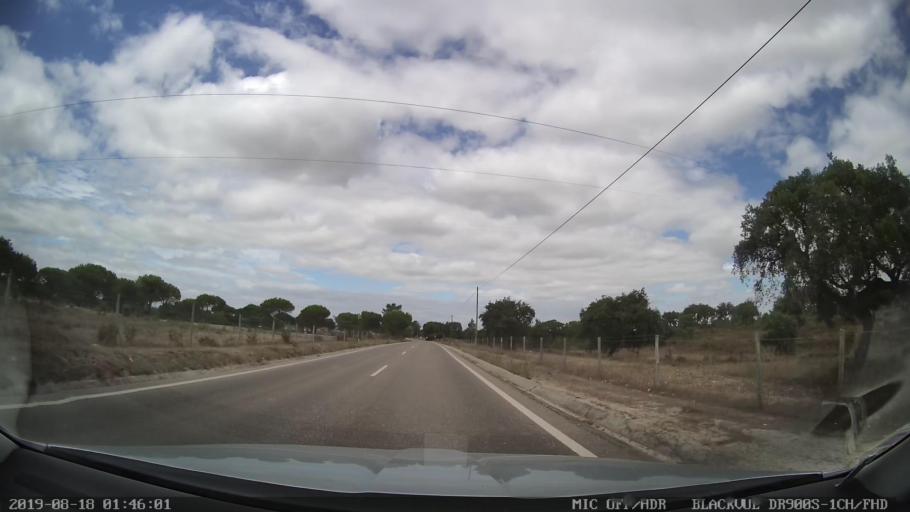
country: PT
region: Santarem
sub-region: Benavente
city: Benavente
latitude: 38.9277
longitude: -8.7772
